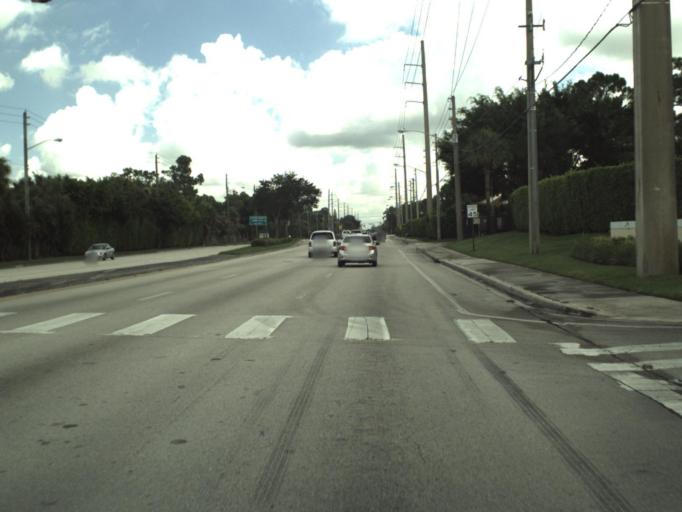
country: US
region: Florida
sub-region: Palm Beach County
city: Royal Palm Estates
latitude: 26.6590
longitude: -80.1452
